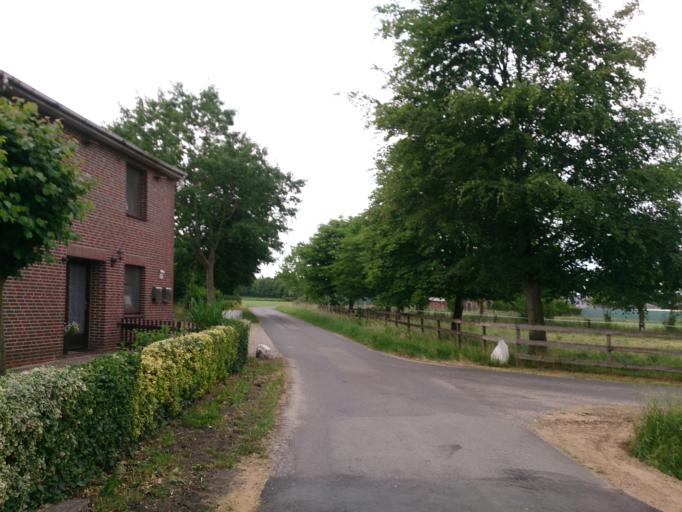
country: DE
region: Schleswig-Holstein
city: Bevern
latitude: 53.7390
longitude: 9.8041
